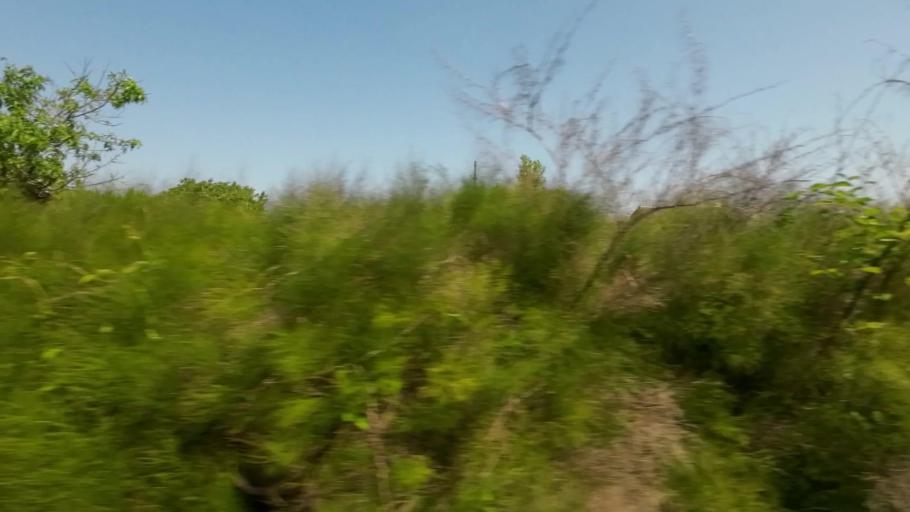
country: JP
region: Ehime
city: Niihama
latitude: 33.9735
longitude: 133.3458
